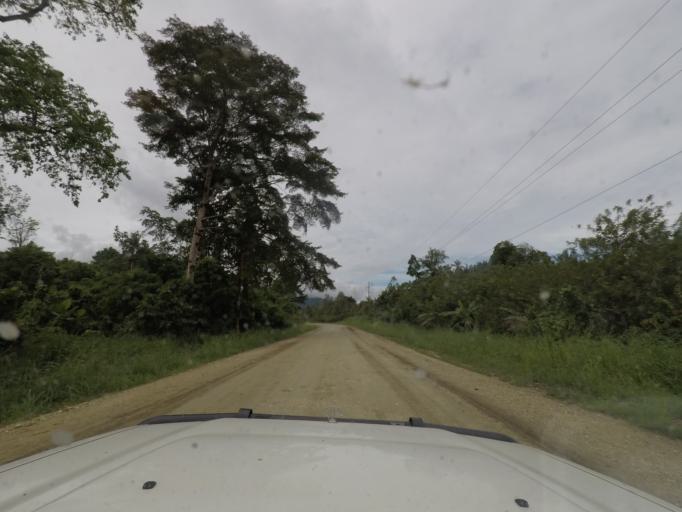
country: PG
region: Eastern Highlands
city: Goroka
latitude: -5.7007
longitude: 145.5407
